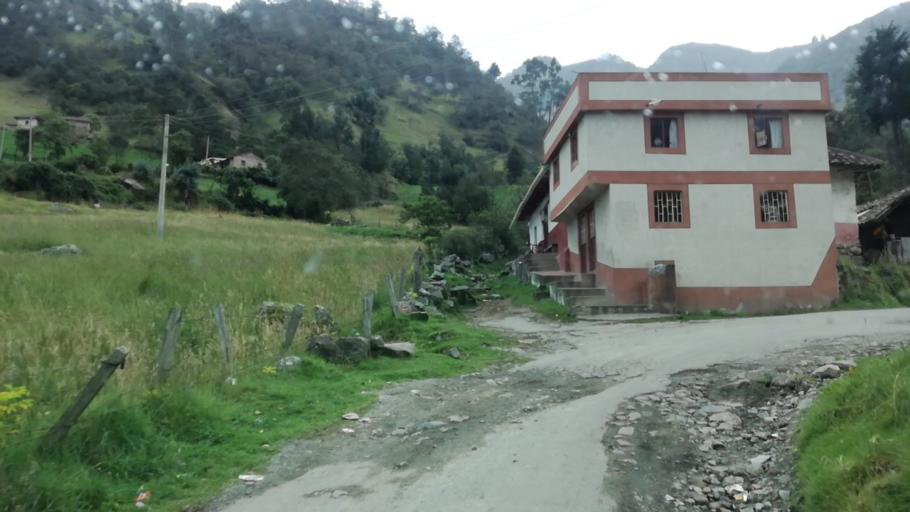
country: CO
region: Boyaca
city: Socha Viejo
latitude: 5.9370
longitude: -72.6906
